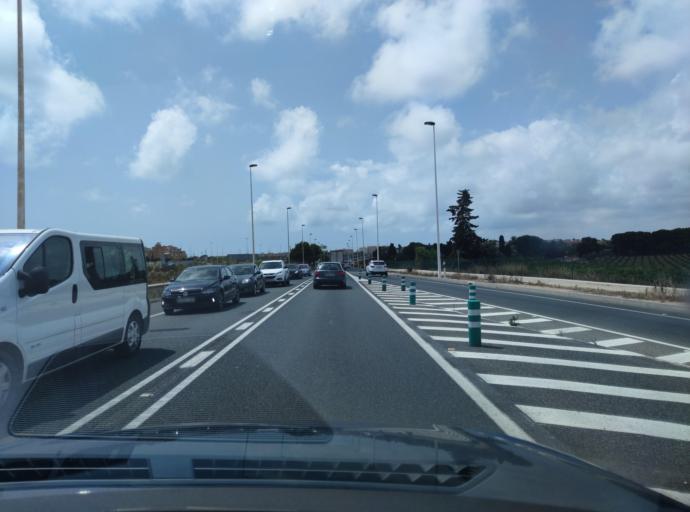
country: ES
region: Valencia
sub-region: Provincia de Alicante
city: Torrevieja
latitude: 37.9604
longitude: -0.7080
